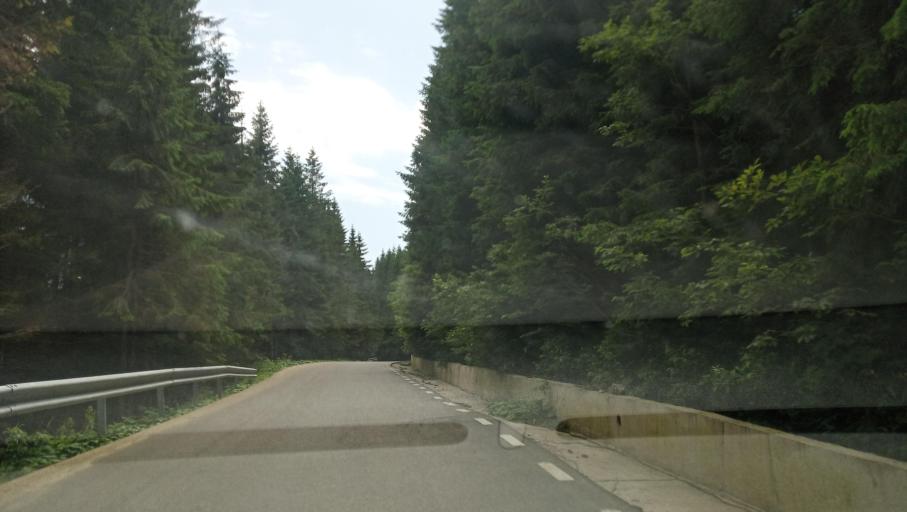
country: RO
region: Dambovita
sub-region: Comuna Moroeni
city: Glod
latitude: 45.3262
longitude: 25.4478
